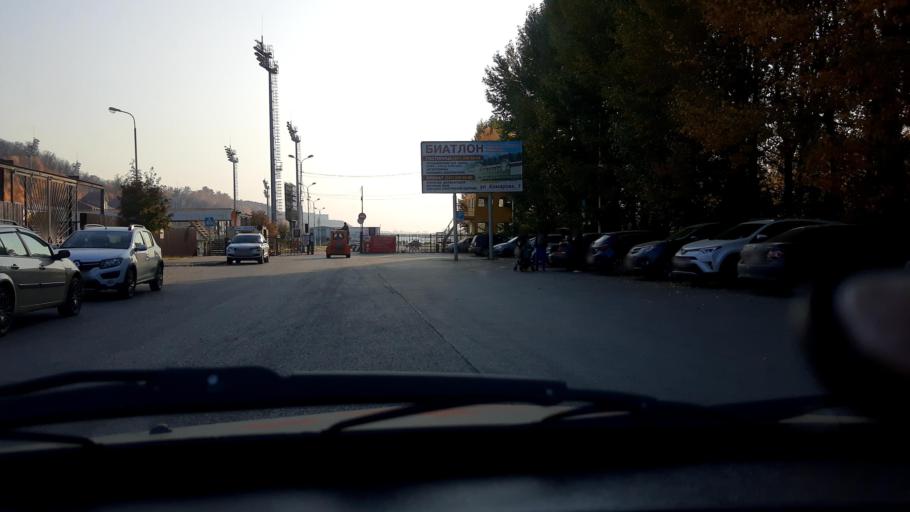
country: RU
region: Bashkortostan
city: Ufa
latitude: 54.8082
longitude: 56.0372
